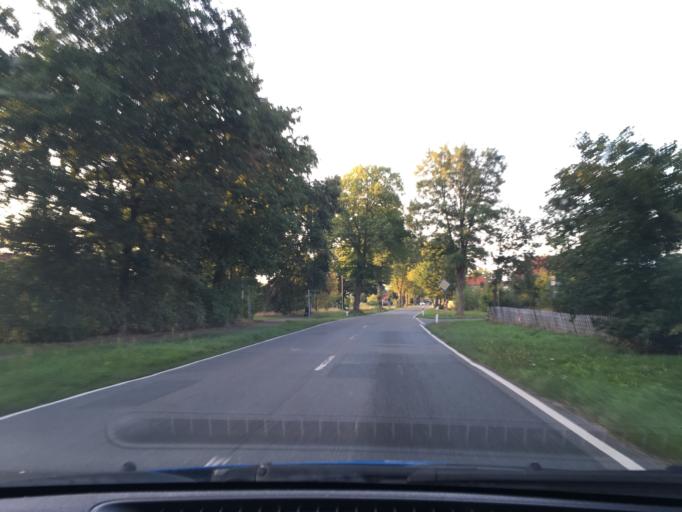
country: DE
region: Lower Saxony
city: Bleckede
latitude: 53.2794
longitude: 10.7411
